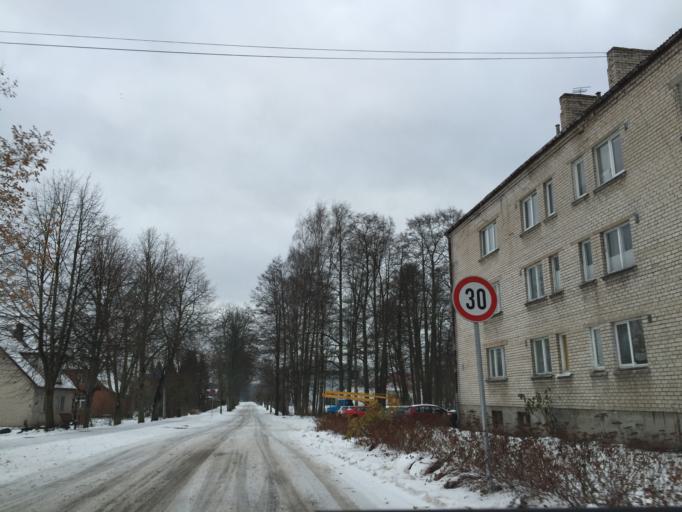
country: LV
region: Saulkrastu
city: Saulkrasti
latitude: 57.2635
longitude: 24.4182
